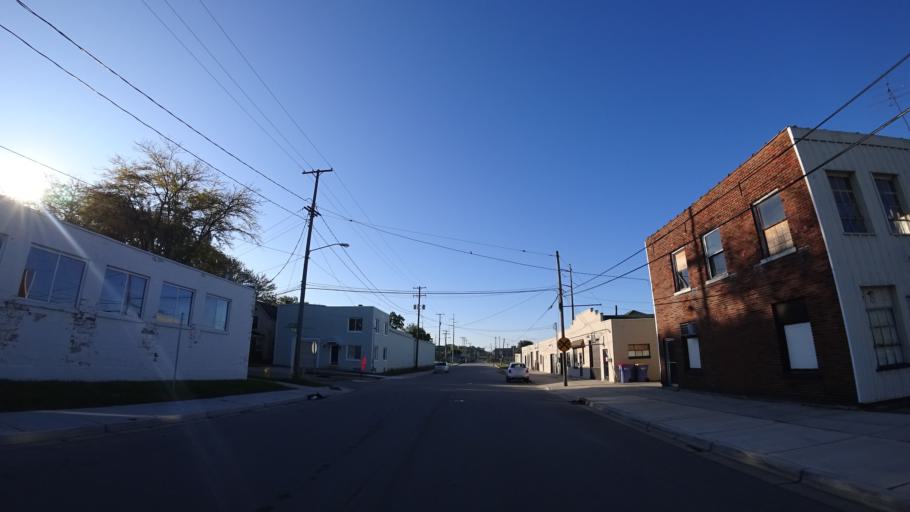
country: US
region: Michigan
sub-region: Kent County
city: Grand Rapids
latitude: 42.9909
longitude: -85.6688
